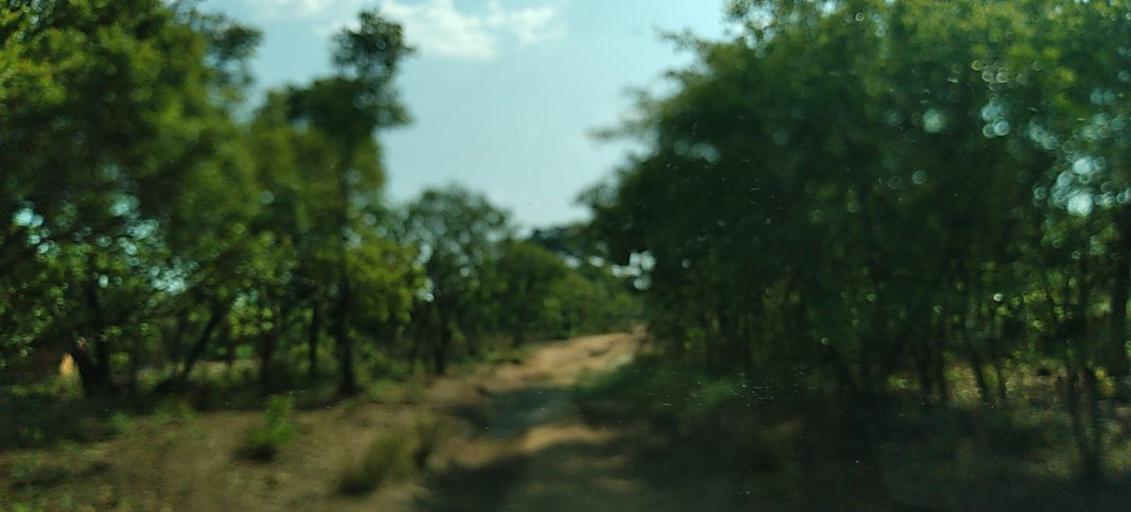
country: ZM
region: North-Western
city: Mwinilunga
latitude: -11.2988
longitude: 24.8536
